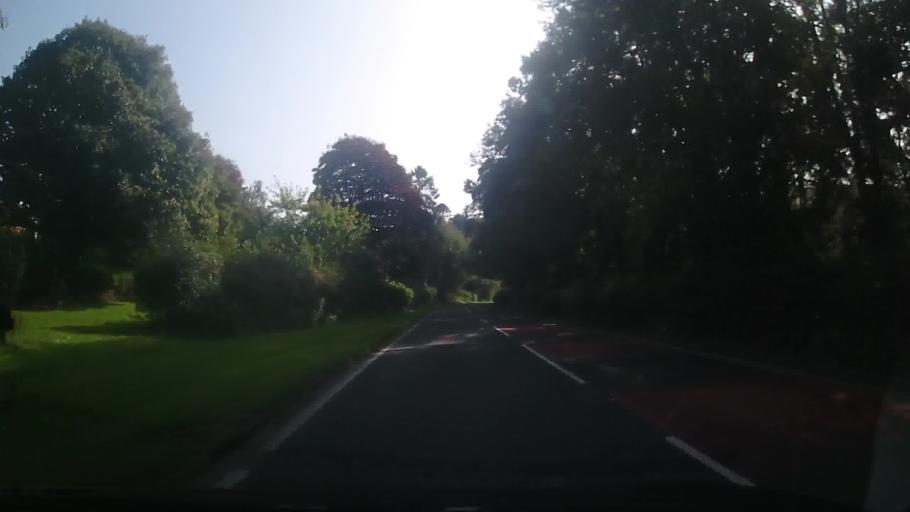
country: GB
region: Wales
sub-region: Sir Powys
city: Rhayader
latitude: 52.2975
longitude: -3.5023
